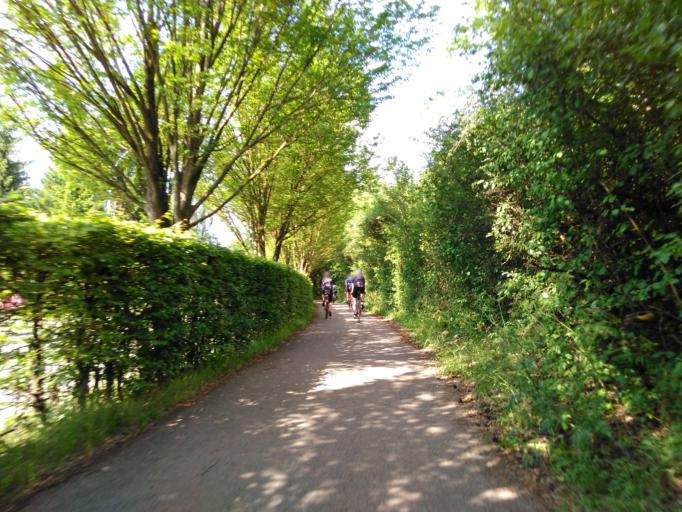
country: LU
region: Luxembourg
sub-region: Canton d'Esch-sur-Alzette
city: Rumelange
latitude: 49.4634
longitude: 6.0363
